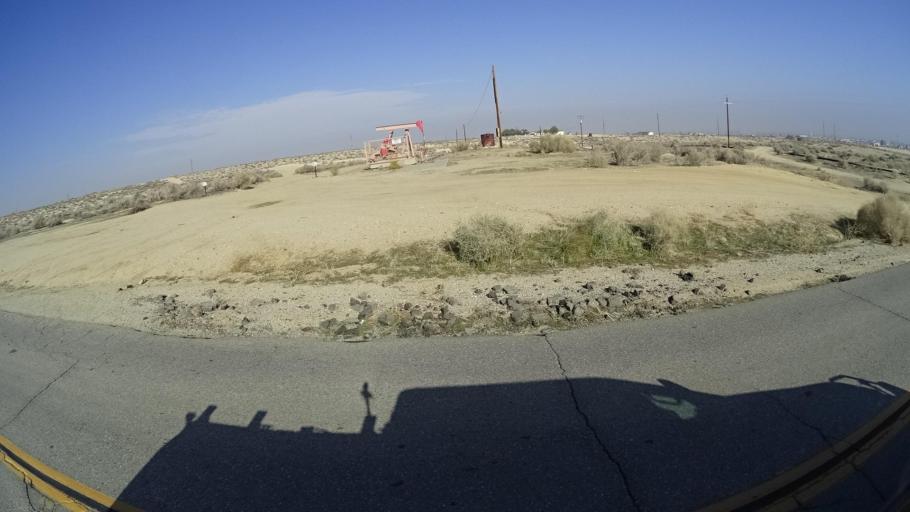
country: US
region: California
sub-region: Kern County
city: Taft Heights
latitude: 35.1408
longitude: -119.4923
